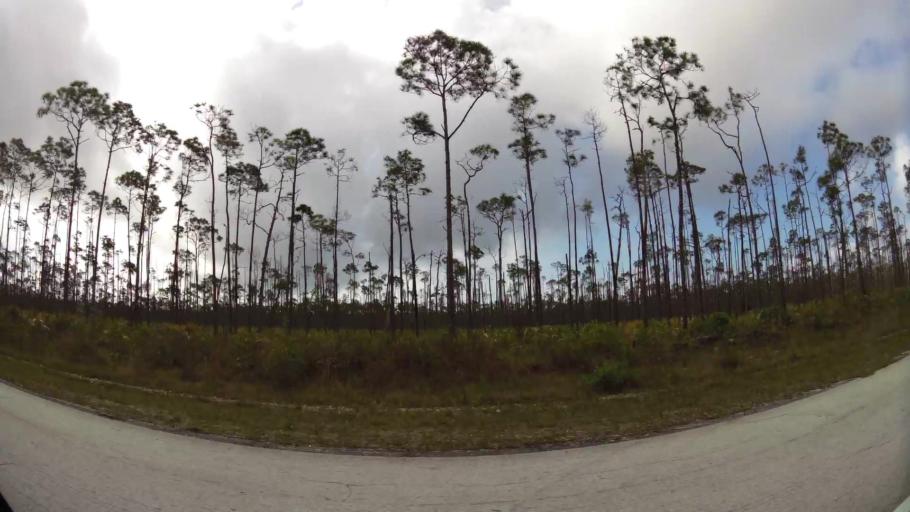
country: BS
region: Freeport
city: Lucaya
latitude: 26.5935
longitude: -78.5493
